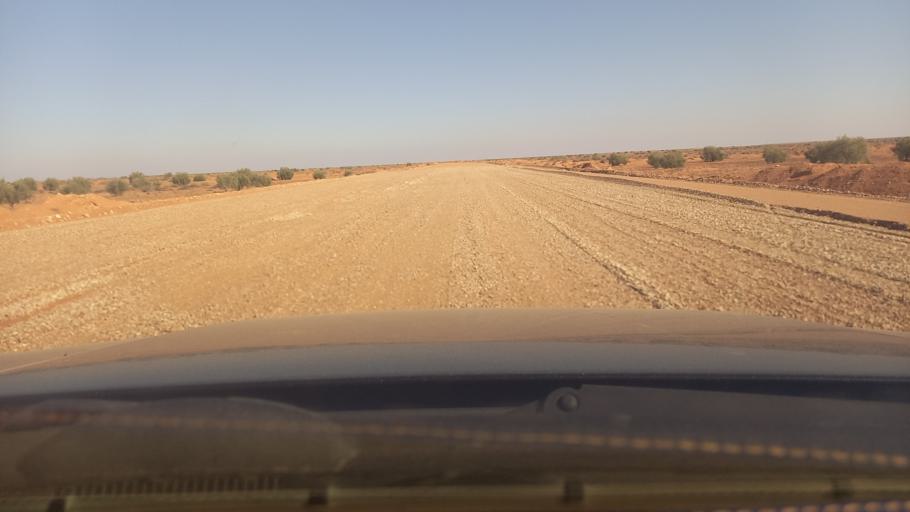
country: TN
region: Madanin
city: Medenine
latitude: 33.1554
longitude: 10.5135
